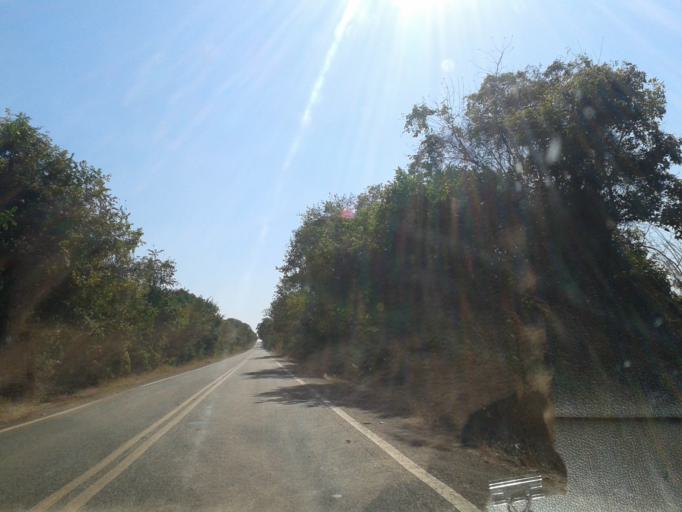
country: BR
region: Goias
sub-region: Mozarlandia
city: Mozarlandia
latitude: -14.4888
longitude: -50.4810
